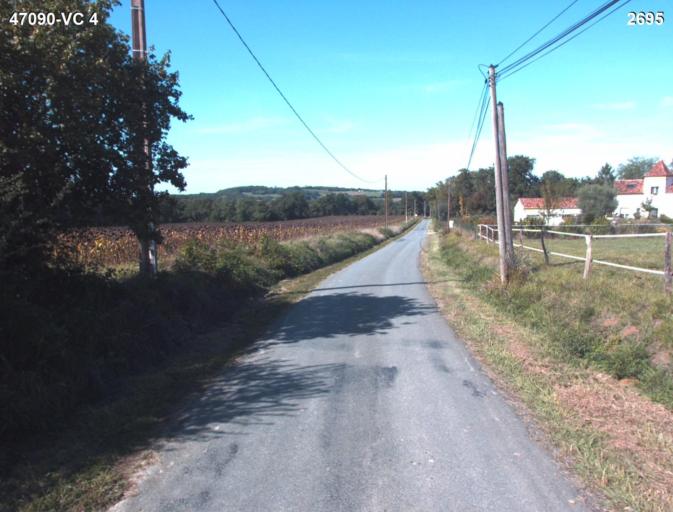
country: FR
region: Aquitaine
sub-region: Departement du Lot-et-Garonne
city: Nerac
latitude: 44.1721
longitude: 0.3704
